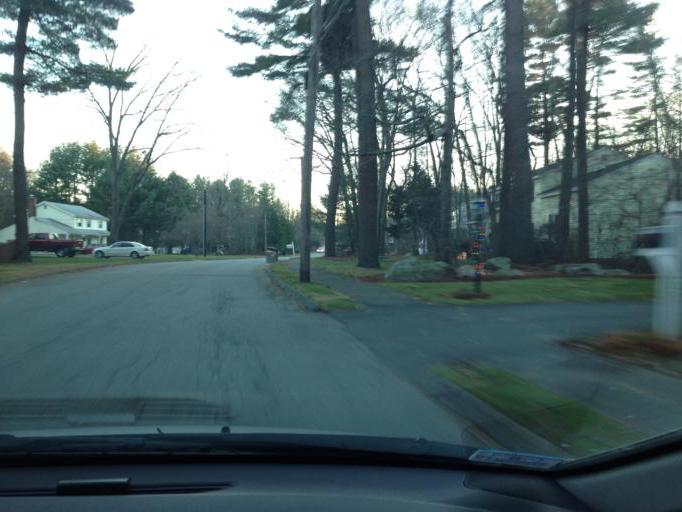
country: US
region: Massachusetts
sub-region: Middlesex County
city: Bedford
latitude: 42.4953
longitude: -71.2721
